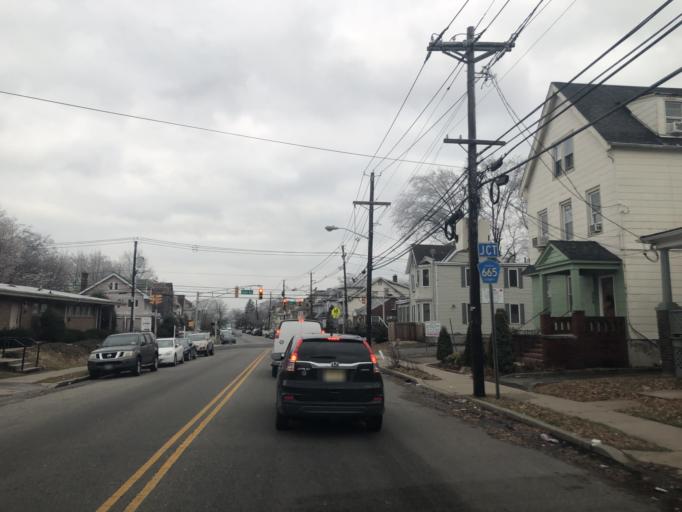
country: US
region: New Jersey
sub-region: Essex County
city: Irvington
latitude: 40.7301
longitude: -74.2400
